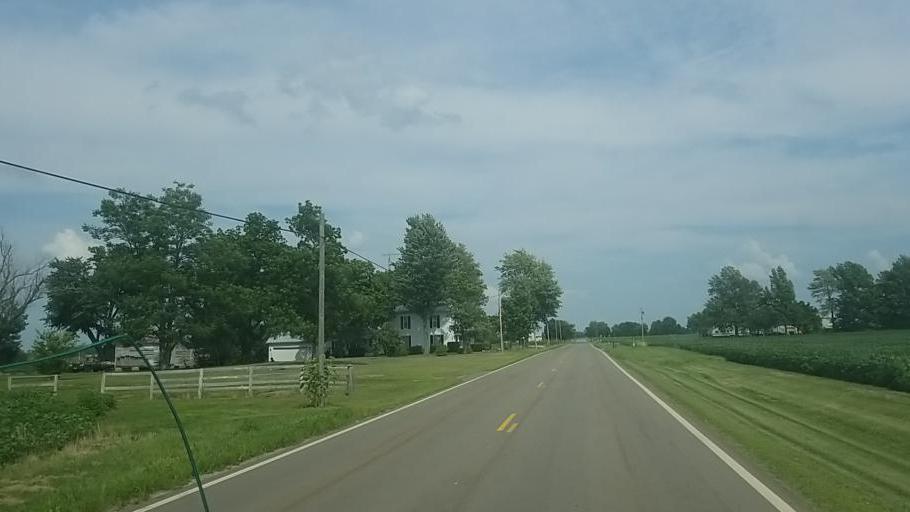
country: US
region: Ohio
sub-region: Hardin County
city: Forest
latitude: 40.8036
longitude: -83.4797
